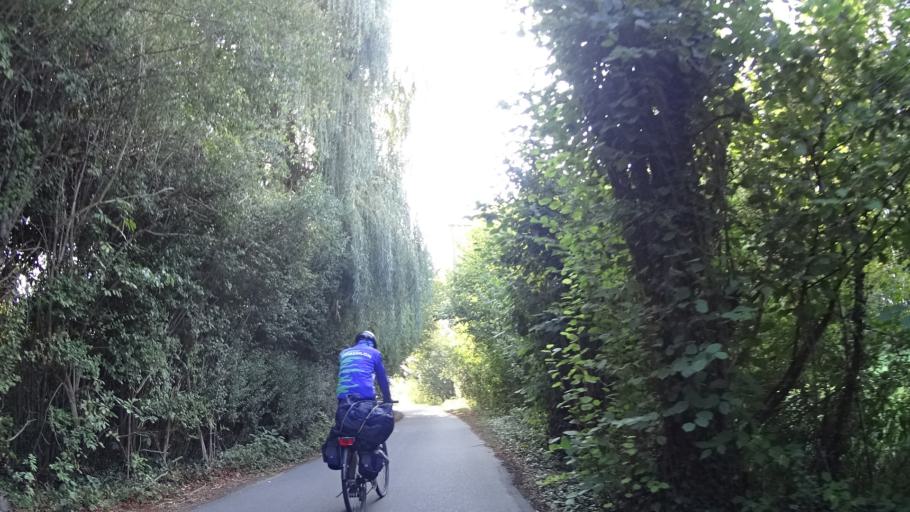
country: DE
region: Baden-Wuerttemberg
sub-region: Karlsruhe Region
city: Ketsch
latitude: 49.3545
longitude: 8.5192
